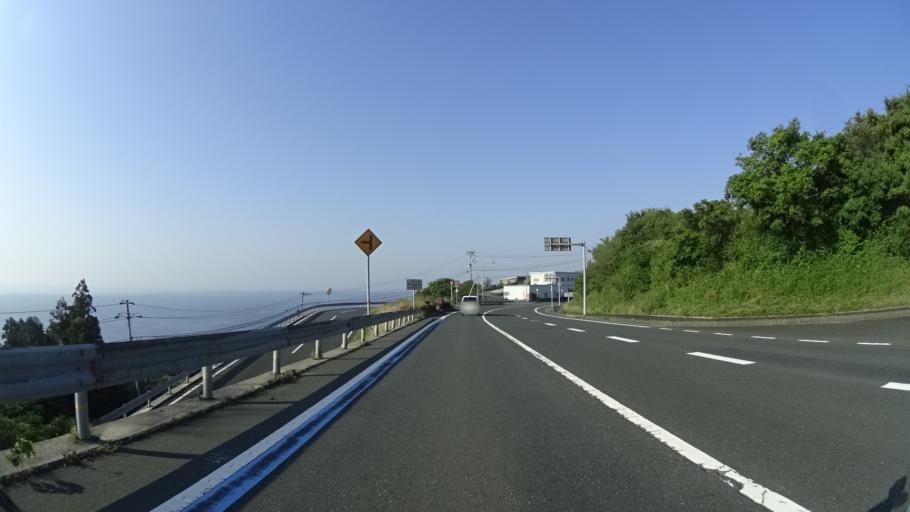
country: JP
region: Ehime
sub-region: Nishiuwa-gun
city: Ikata-cho
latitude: 33.4050
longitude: 132.1715
